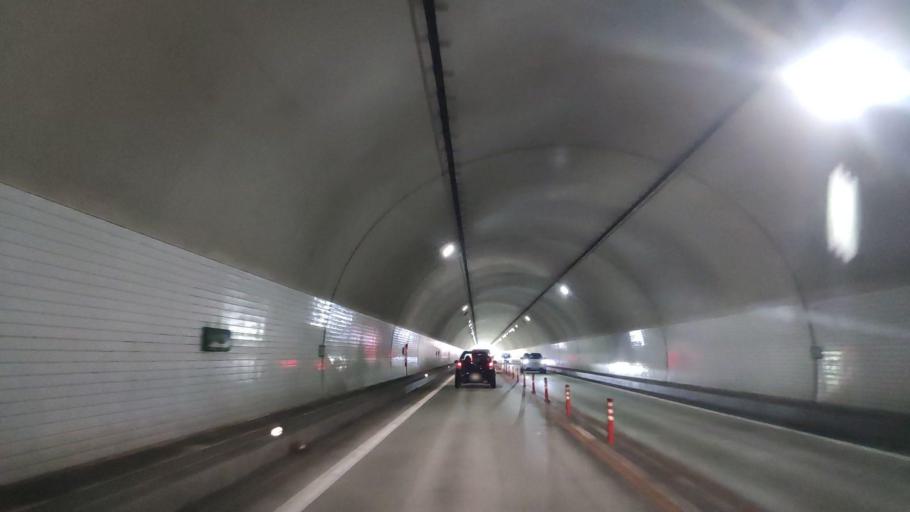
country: JP
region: Akita
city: Takanosu
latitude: 40.2213
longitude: 140.4297
